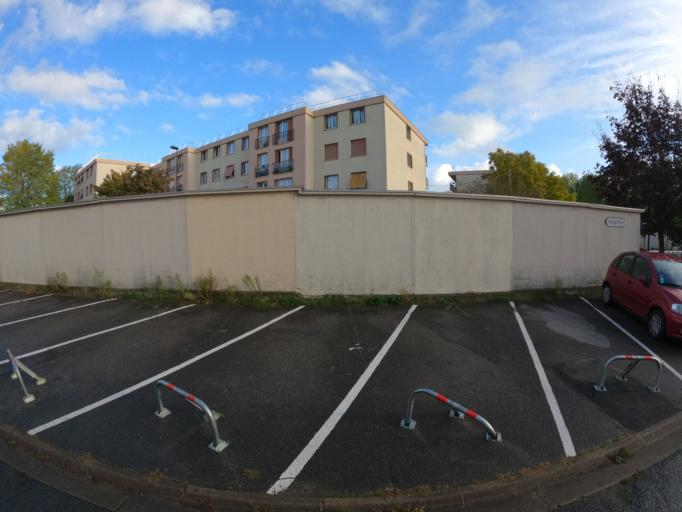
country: FR
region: Ile-de-France
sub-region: Departement de Seine-et-Marne
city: Brou-sur-Chantereine
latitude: 48.8837
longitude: 2.6304
